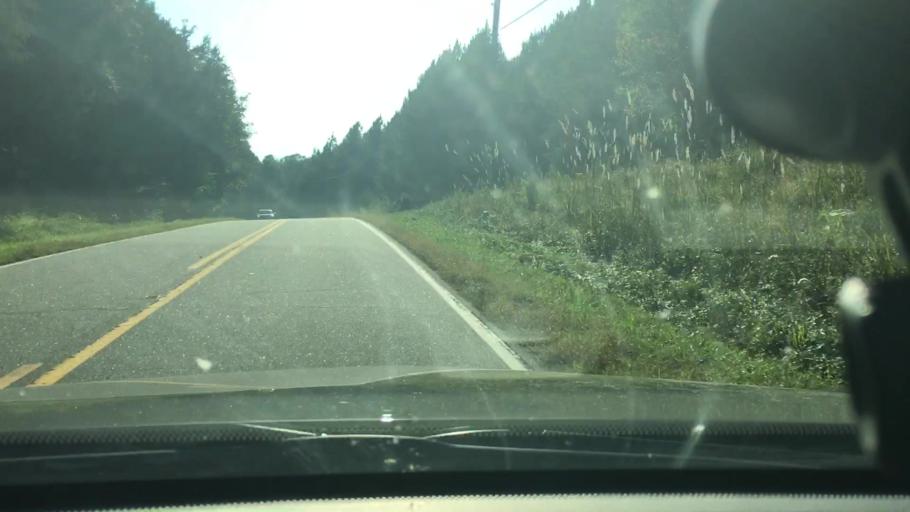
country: US
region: North Carolina
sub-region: Rutherford County
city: Rutherfordton
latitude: 35.3341
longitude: -82.0240
